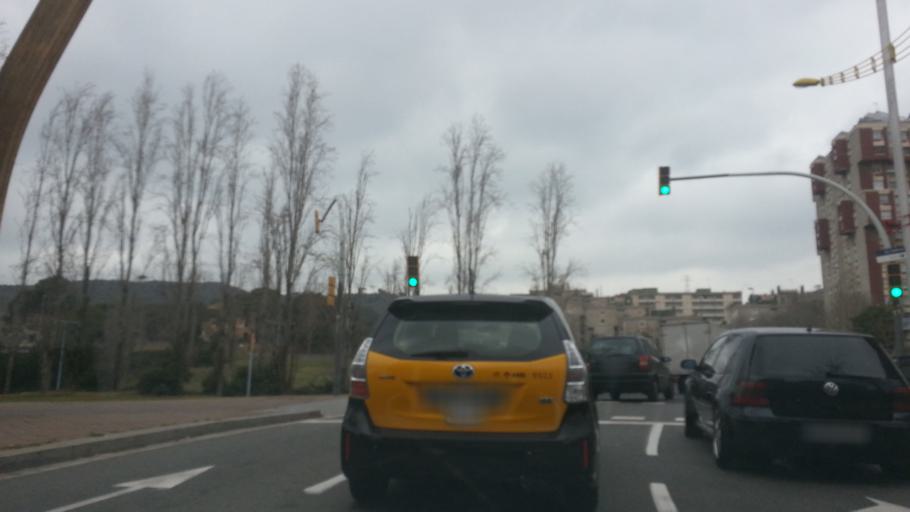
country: ES
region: Catalonia
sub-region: Provincia de Barcelona
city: Nou Barris
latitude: 41.4398
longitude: 2.1633
